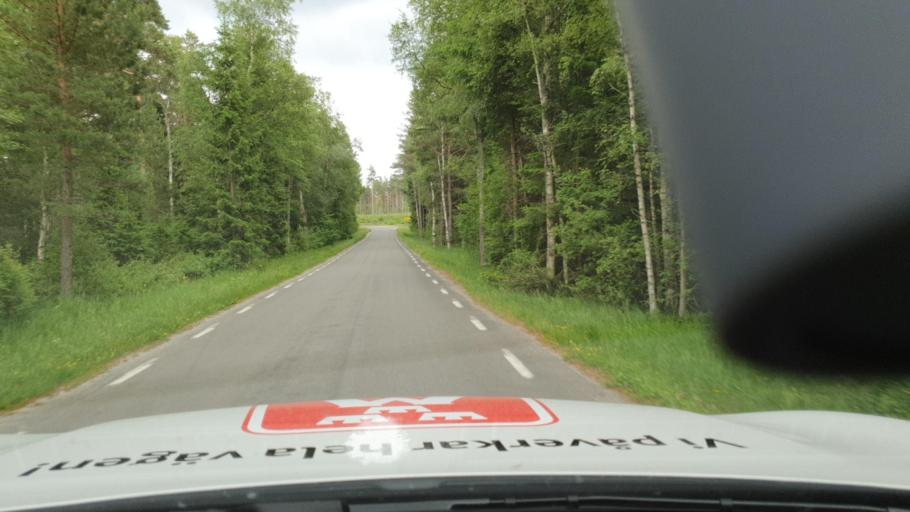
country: SE
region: Vaestra Goetaland
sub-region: Tidaholms Kommun
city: Olofstorp
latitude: 58.1771
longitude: 14.1460
